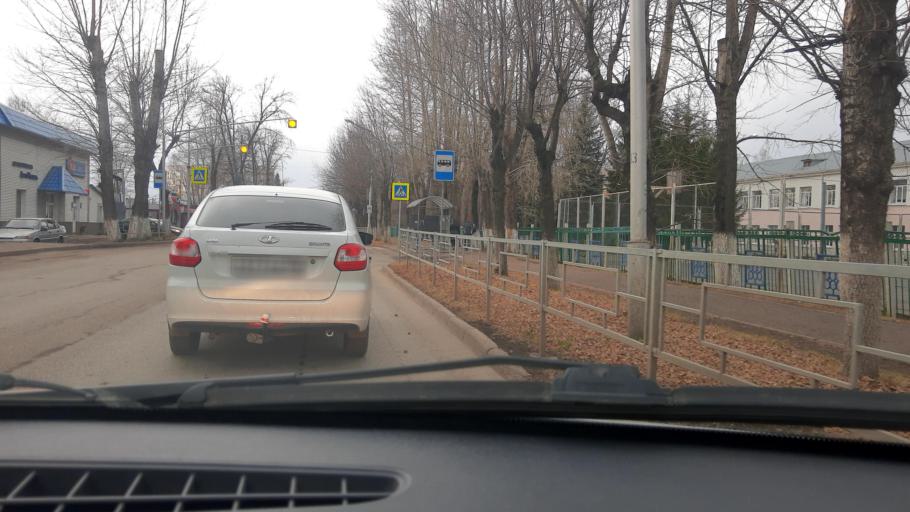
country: RU
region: Bashkortostan
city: Avdon
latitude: 54.6968
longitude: 55.8247
